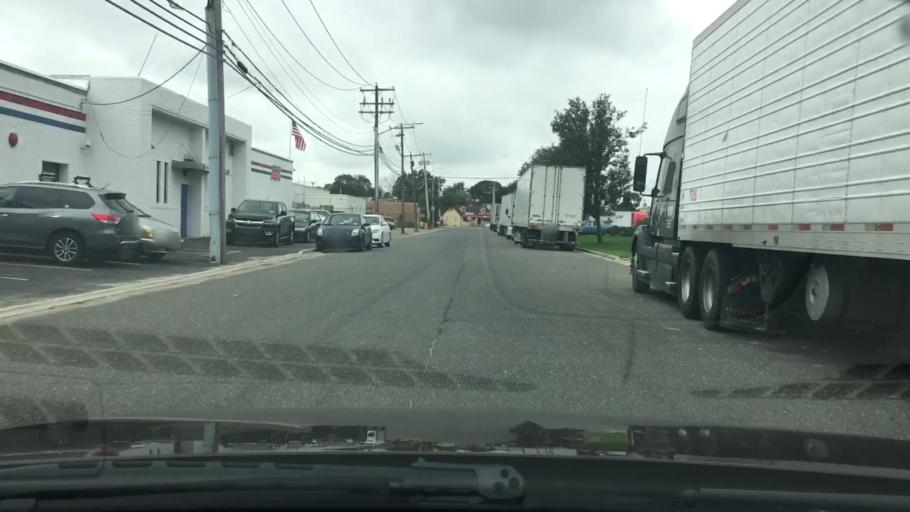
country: US
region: New York
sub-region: Nassau County
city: Hicksville
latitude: 40.7587
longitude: -73.5098
